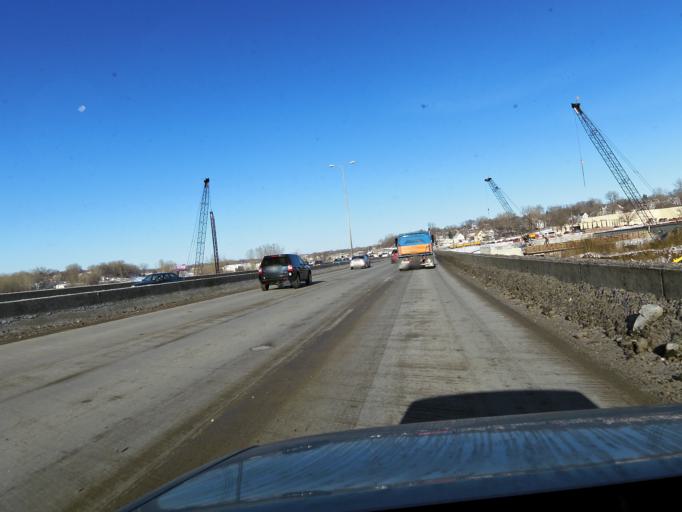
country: US
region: Minnesota
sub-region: Ramsey County
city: Saint Paul
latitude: 44.9668
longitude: -93.0903
